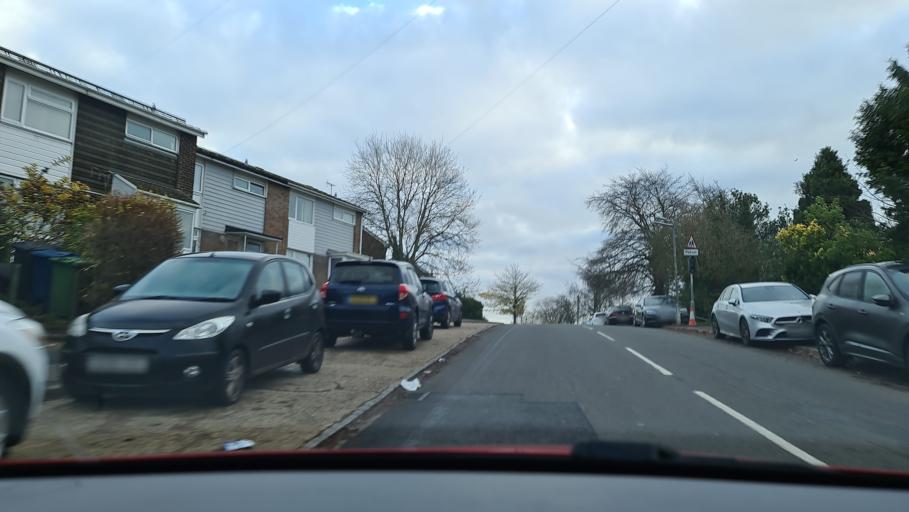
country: GB
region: England
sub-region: Buckinghamshire
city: High Wycombe
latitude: 51.6384
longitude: -0.7643
